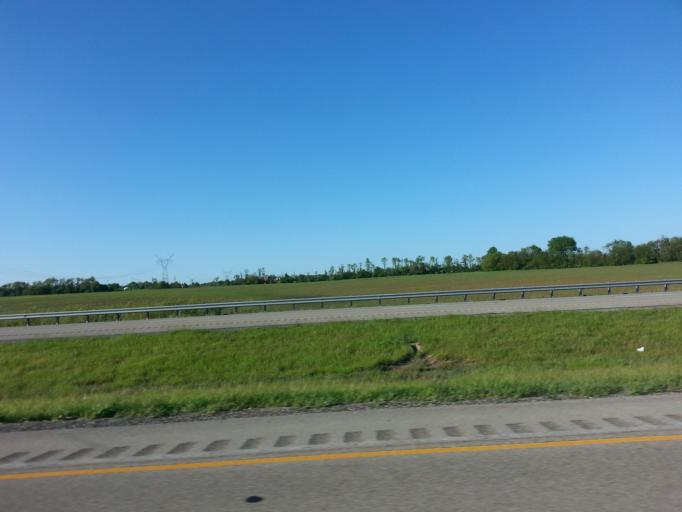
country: US
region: Illinois
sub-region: McLean County
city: Downs
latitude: 40.3863
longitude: -88.8679
